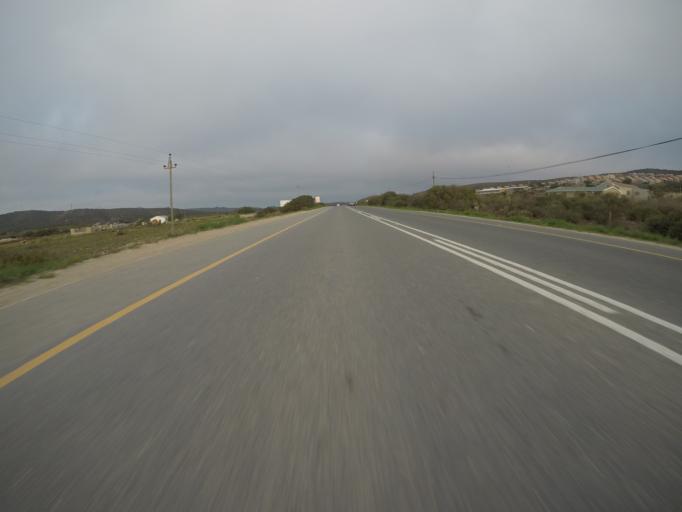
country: ZA
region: Western Cape
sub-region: Eden District Municipality
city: Mossel Bay
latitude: -34.1139
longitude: 22.0828
